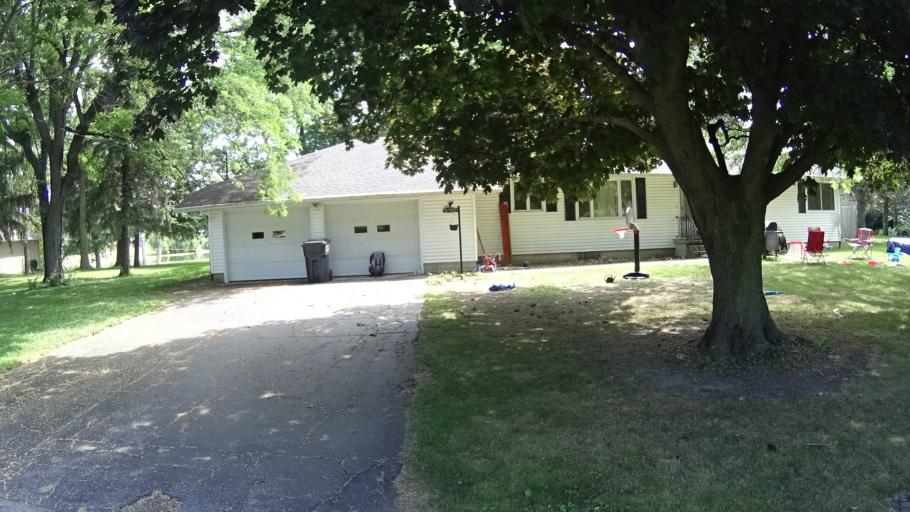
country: US
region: Ohio
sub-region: Erie County
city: Sandusky
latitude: 41.3988
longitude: -82.8063
